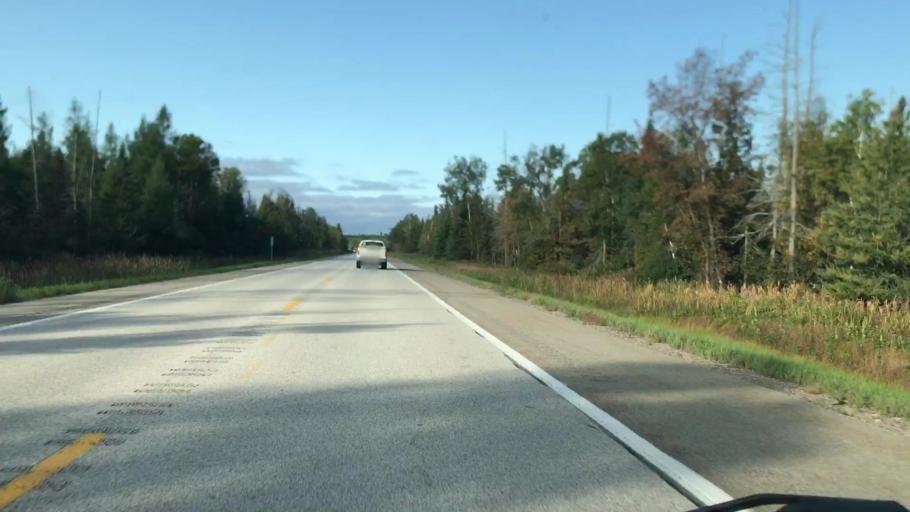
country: US
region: Michigan
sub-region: Luce County
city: Newberry
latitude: 46.3211
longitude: -85.1838
